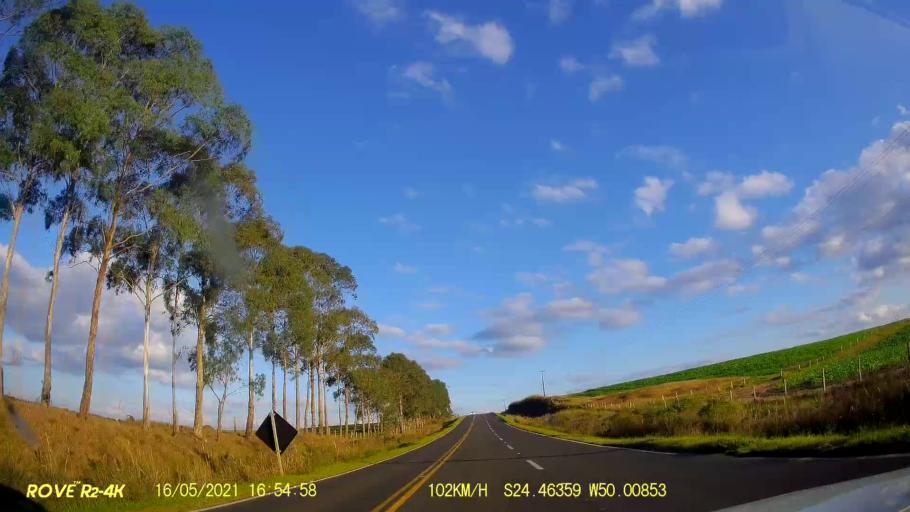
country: BR
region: Parana
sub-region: Pirai Do Sul
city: Pirai do Sul
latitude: -24.4633
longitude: -50.0085
